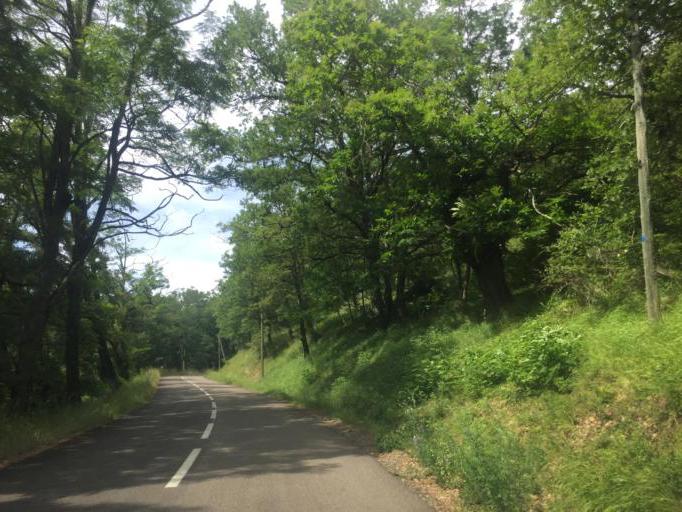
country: FR
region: Rhone-Alpes
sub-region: Departement de l'Ardeche
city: Villeneuve-de-Berg
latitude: 44.6145
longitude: 4.5417
